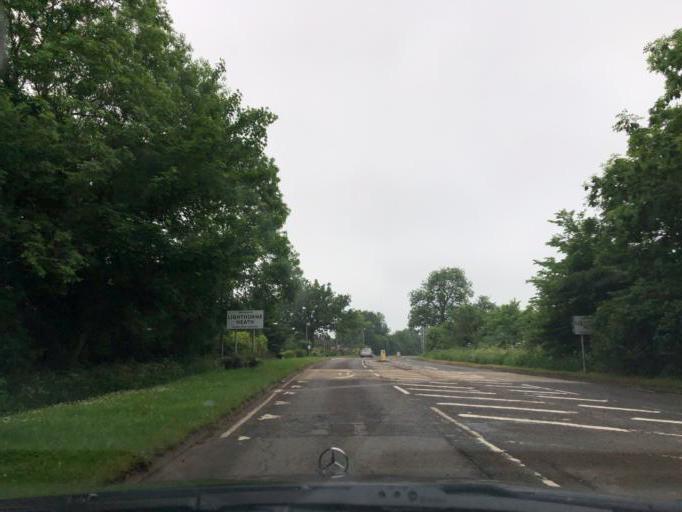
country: GB
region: England
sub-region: Warwickshire
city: Harbury
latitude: 52.1979
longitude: -1.4830
